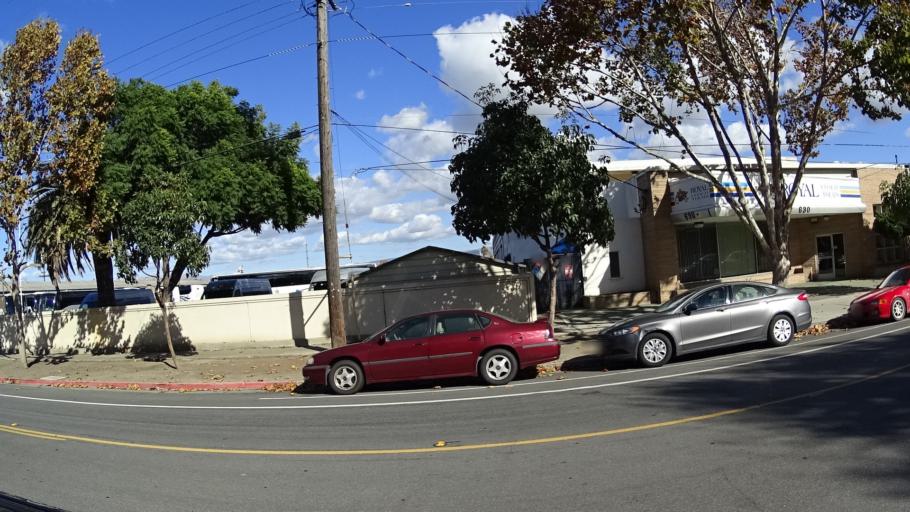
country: US
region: California
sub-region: Santa Clara County
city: San Jose
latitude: 37.3395
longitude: -121.9122
